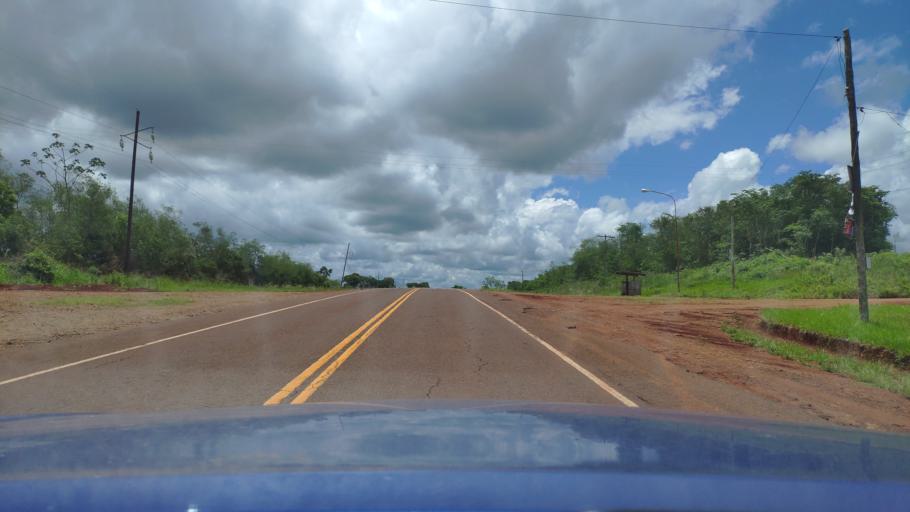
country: AR
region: Misiones
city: Picada Gobernador Lopez
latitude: -27.6823
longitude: -55.2817
